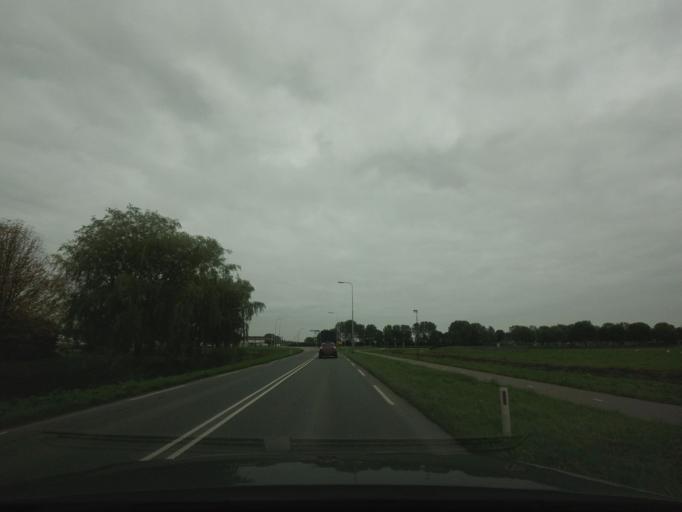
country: NL
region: North Holland
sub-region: Gemeente Heerhugowaard
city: Heerhugowaard
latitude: 52.6723
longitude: 4.8946
